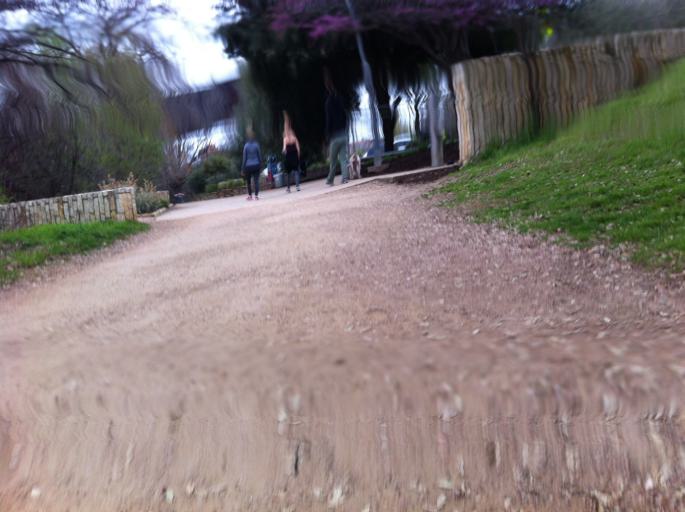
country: US
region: Texas
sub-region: Travis County
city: Austin
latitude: 30.2651
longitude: -97.7570
